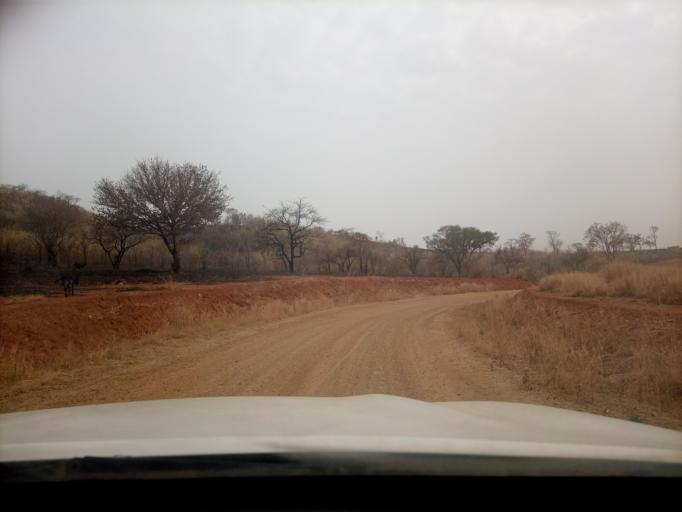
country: ET
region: Oromiya
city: Mendi
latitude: 10.1983
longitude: 35.0663
